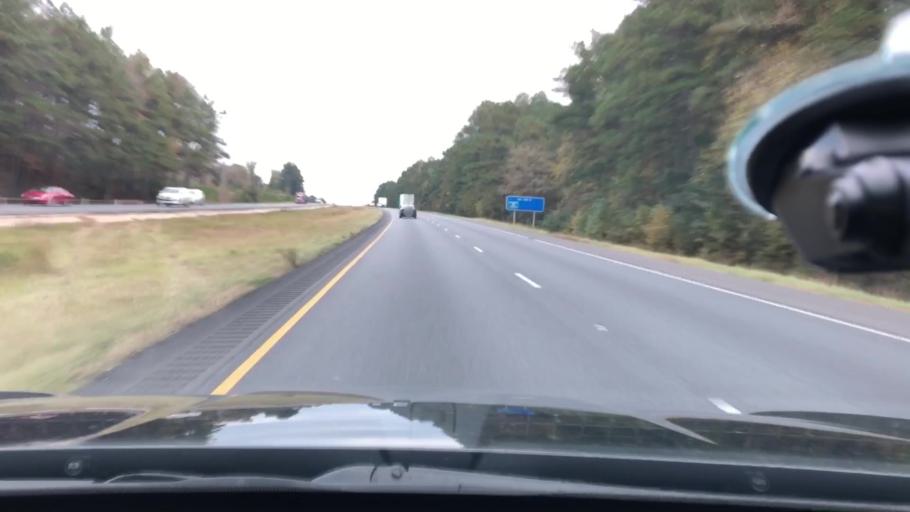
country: US
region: Arkansas
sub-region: Clark County
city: Arkadelphia
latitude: 34.2188
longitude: -93.0243
